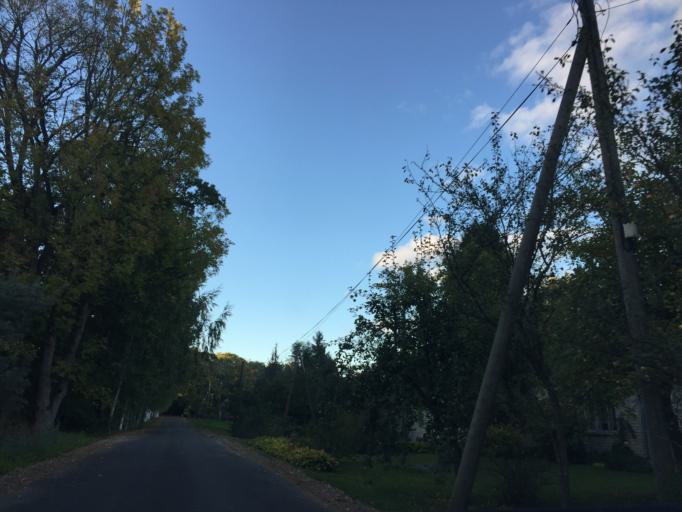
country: LV
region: Varaklani
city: Varaklani
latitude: 56.6063
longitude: 26.7792
